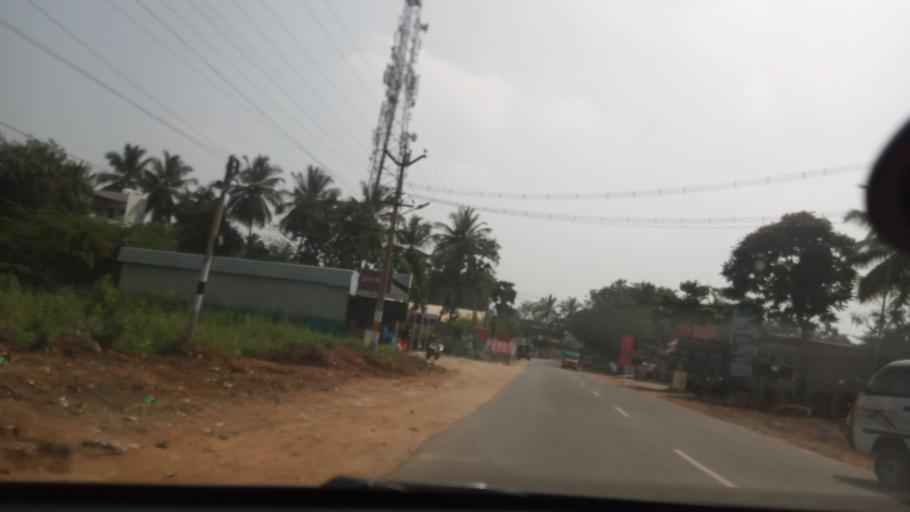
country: IN
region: Tamil Nadu
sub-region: Coimbatore
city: Perur
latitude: 11.0195
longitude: 76.8818
